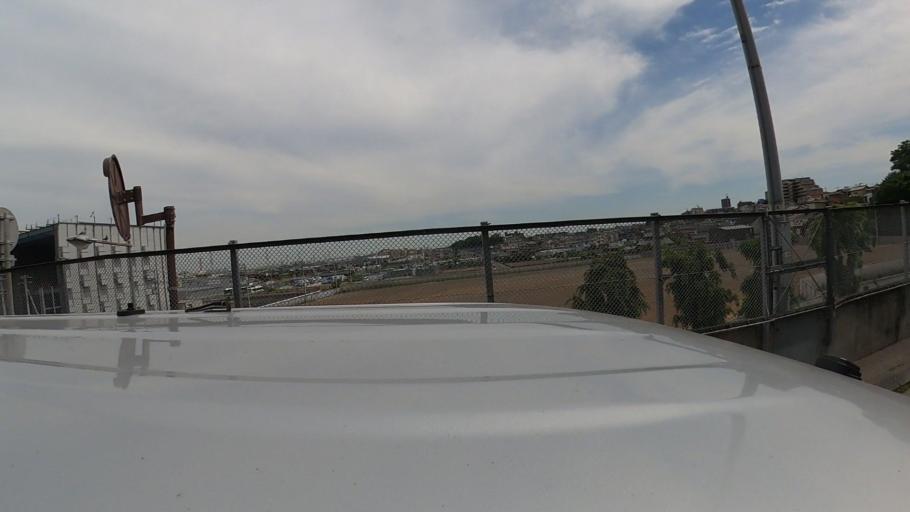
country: JP
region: Saitama
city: Wako
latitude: 35.8007
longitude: 139.6195
